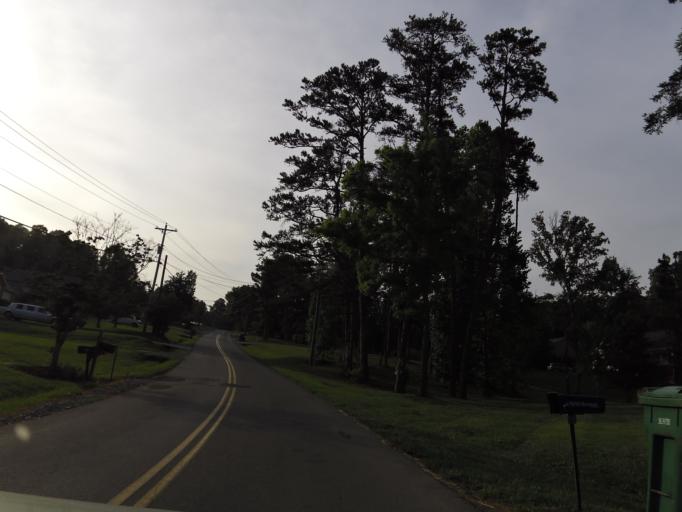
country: US
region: Tennessee
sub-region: Sevier County
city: Seymour
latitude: 35.8643
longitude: -83.7904
